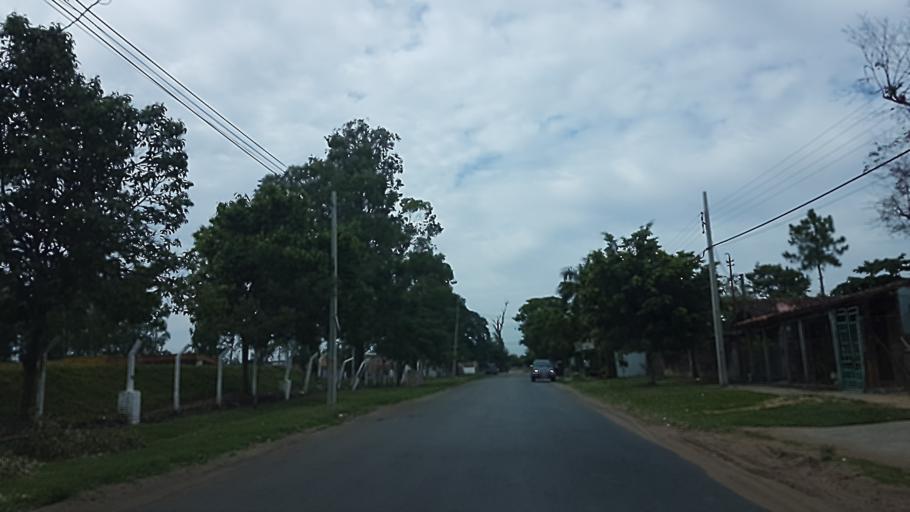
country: PY
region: Central
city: Colonia Mariano Roque Alonso
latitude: -25.2166
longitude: -57.5369
